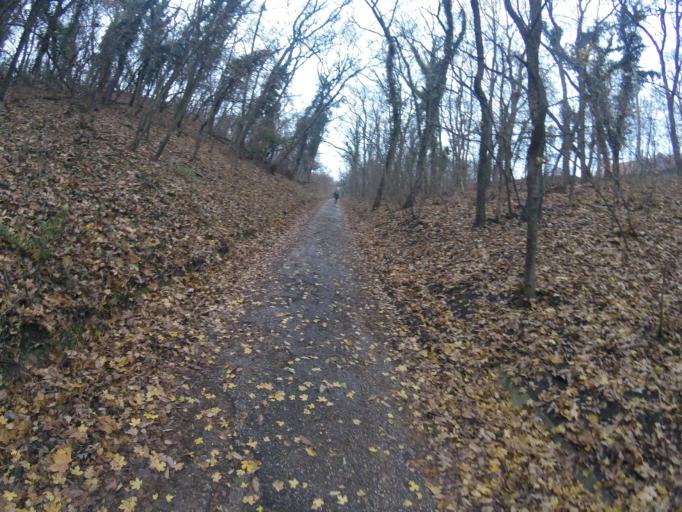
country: HU
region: Veszprem
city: Tihany
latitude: 46.8983
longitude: 17.8646
